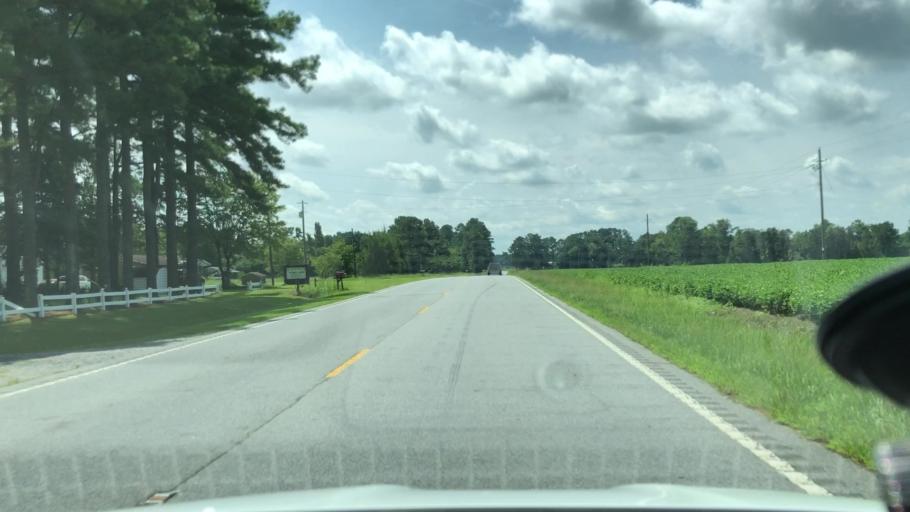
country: US
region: North Carolina
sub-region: Beaufort County
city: Washington
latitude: 35.6603
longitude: -77.0729
